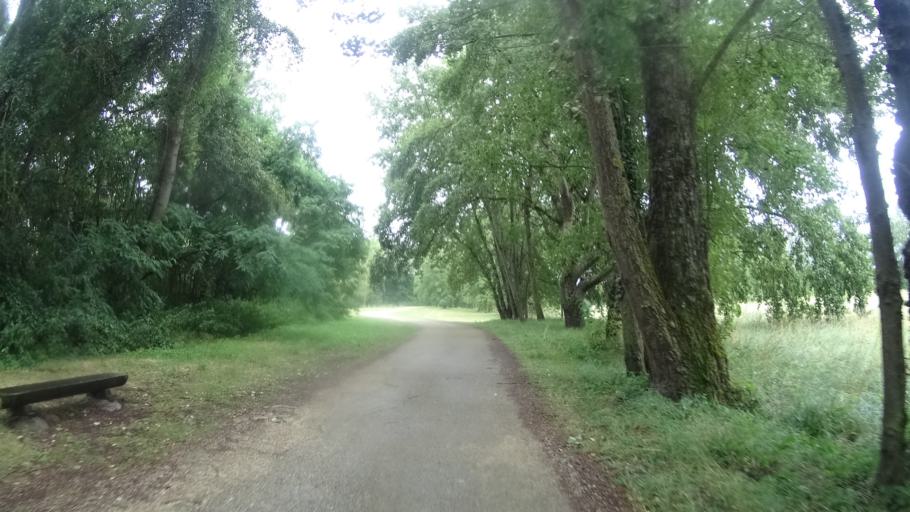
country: FR
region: Centre
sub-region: Departement du Loiret
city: Saint-Jean-de-Braye
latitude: 47.8993
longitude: 1.9643
